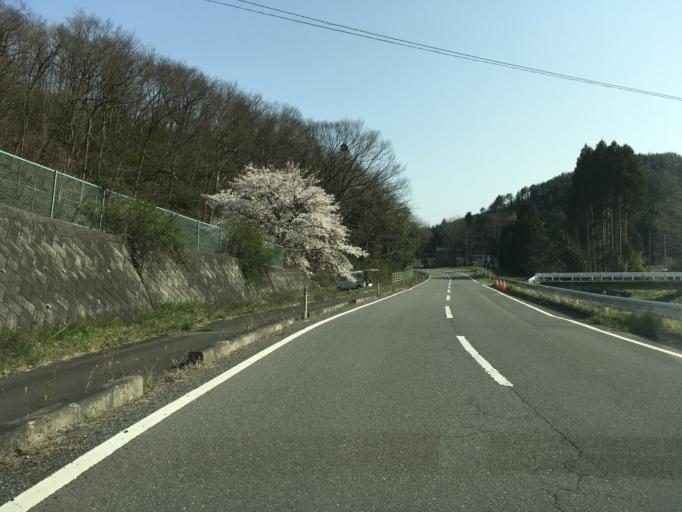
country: JP
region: Iwate
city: Ichinoseki
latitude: 38.7929
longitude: 141.3219
